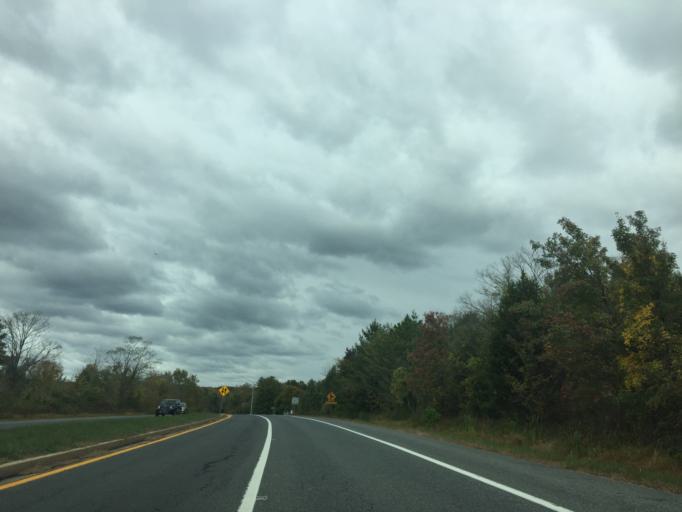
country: US
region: Maryland
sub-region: Harford County
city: Riverside
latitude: 39.4885
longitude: -76.2544
